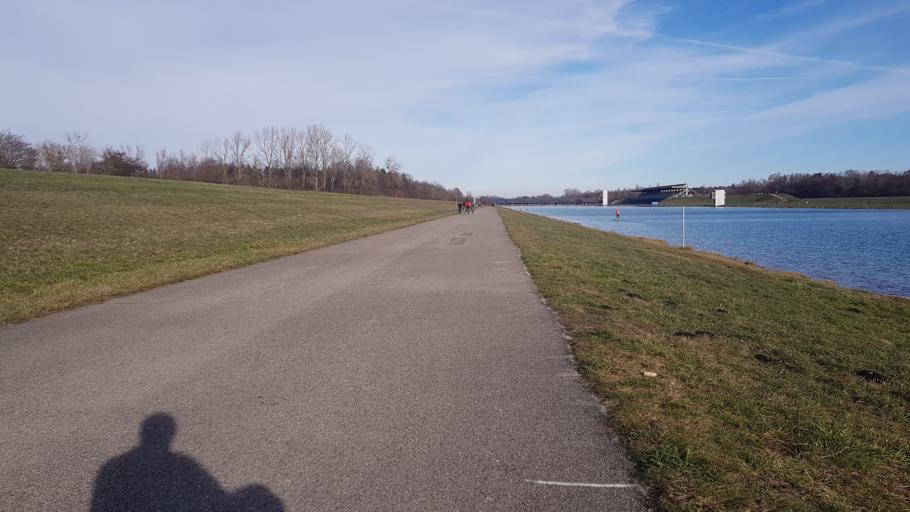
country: DE
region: Bavaria
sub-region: Upper Bavaria
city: Oberschleissheim
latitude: 48.2427
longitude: 11.5136
